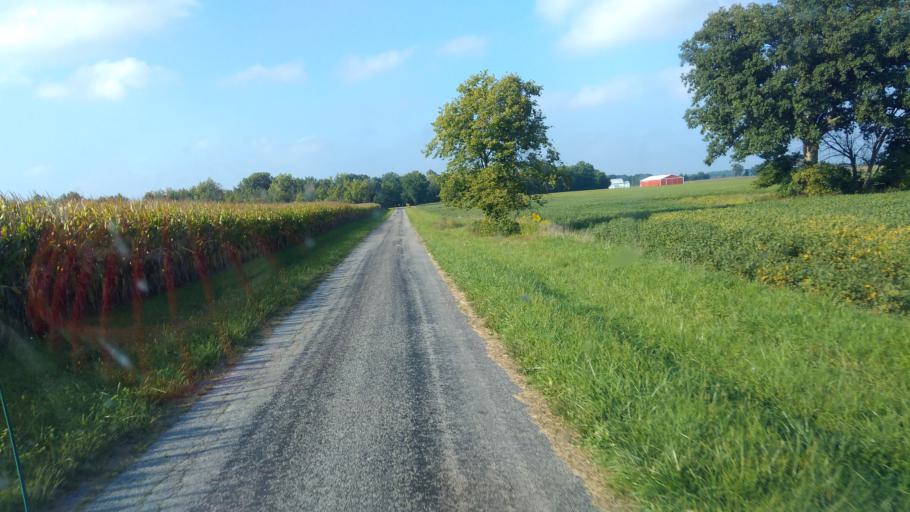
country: US
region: Ohio
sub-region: Wyandot County
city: Upper Sandusky
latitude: 40.7680
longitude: -83.3621
